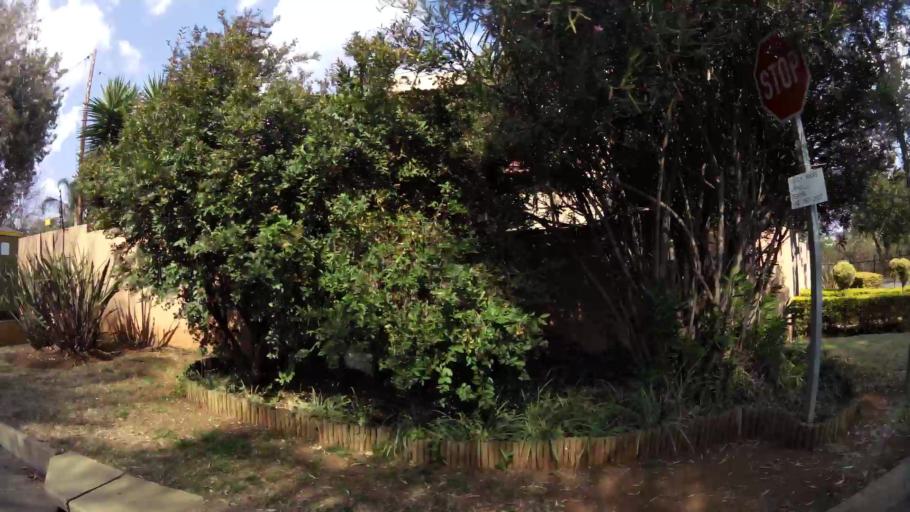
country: ZA
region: Gauteng
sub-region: City of Tshwane Metropolitan Municipality
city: Pretoria
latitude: -25.7951
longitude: 28.3258
